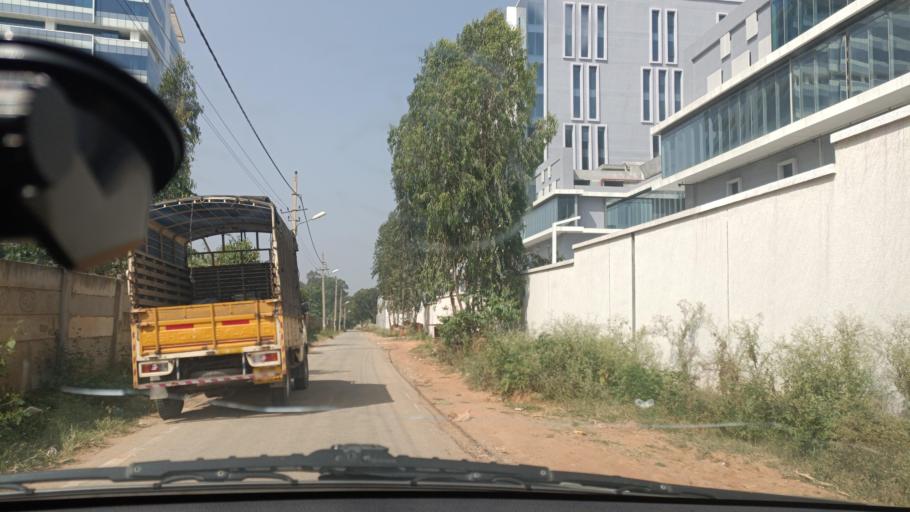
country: IN
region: Karnataka
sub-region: Bangalore Urban
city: Yelahanka
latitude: 13.1157
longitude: 77.6064
